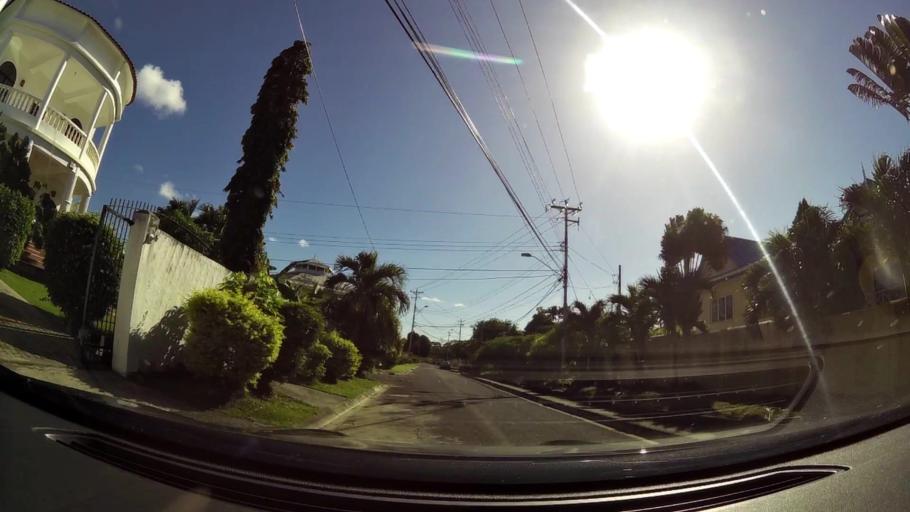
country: TT
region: Tobago
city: Scarborough
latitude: 11.1591
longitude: -60.8268
